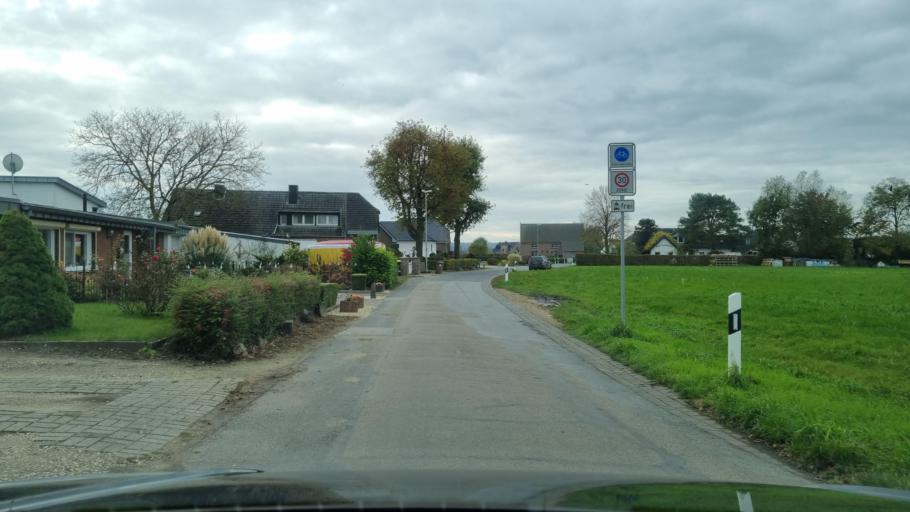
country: DE
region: North Rhine-Westphalia
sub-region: Regierungsbezirk Dusseldorf
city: Kleve
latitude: 51.8298
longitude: 6.1145
